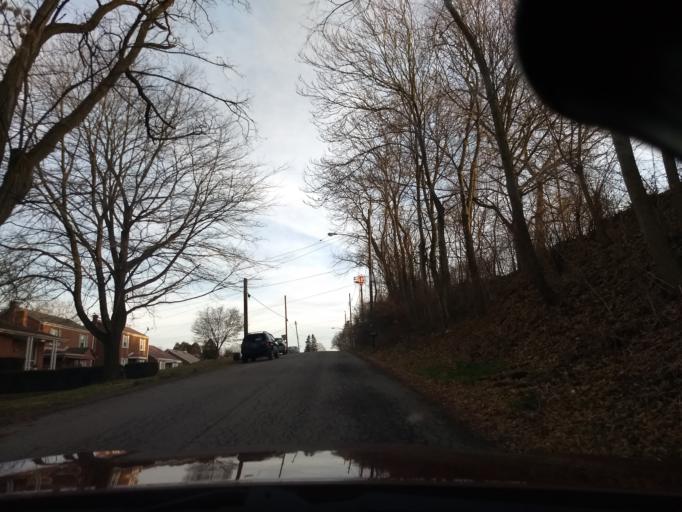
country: US
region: Pennsylvania
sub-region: Allegheny County
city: Dravosburg
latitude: 40.3550
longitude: -79.9104
